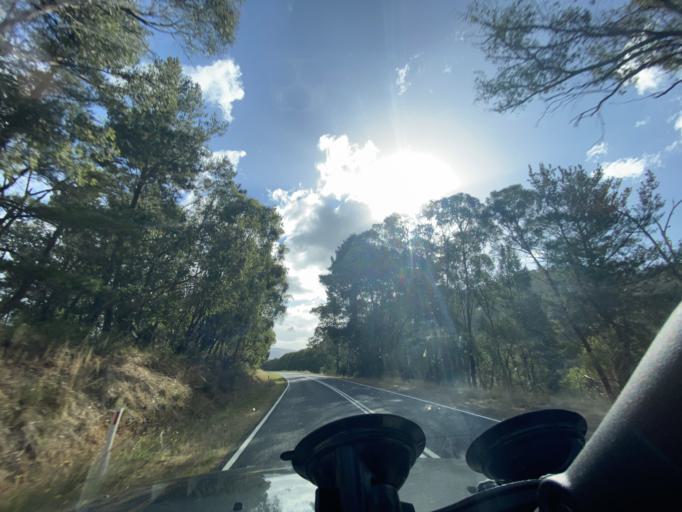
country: AU
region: Victoria
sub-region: Murrindindi
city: Kinglake West
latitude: -37.3234
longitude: 145.3210
